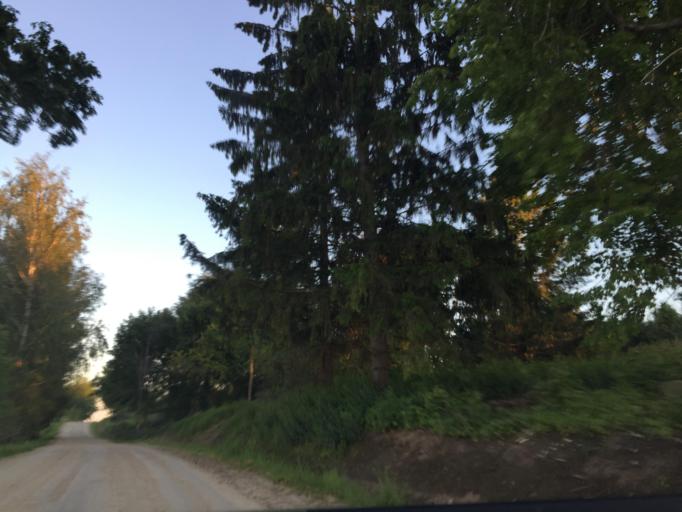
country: LV
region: Rezekne
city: Rezekne
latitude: 56.3641
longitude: 27.4115
